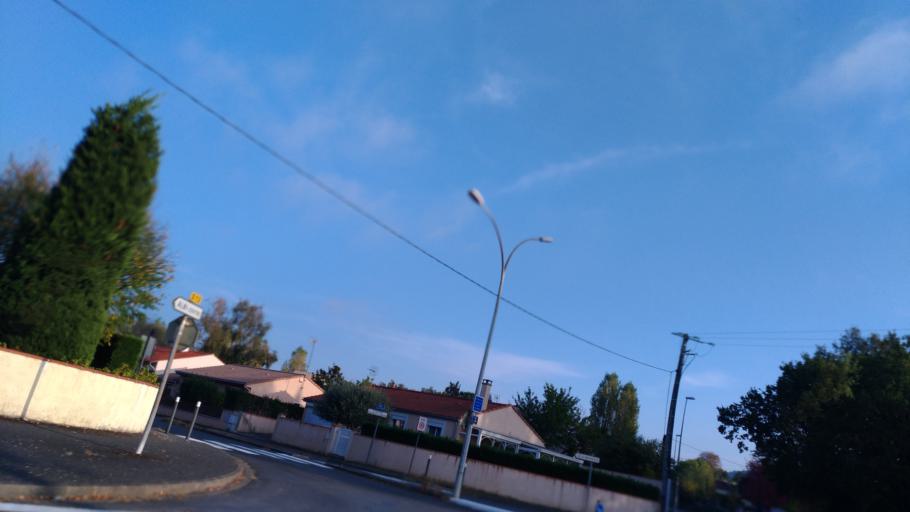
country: FR
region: Midi-Pyrenees
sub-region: Departement du Tarn
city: Puygouzon
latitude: 43.9159
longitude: 2.1675
